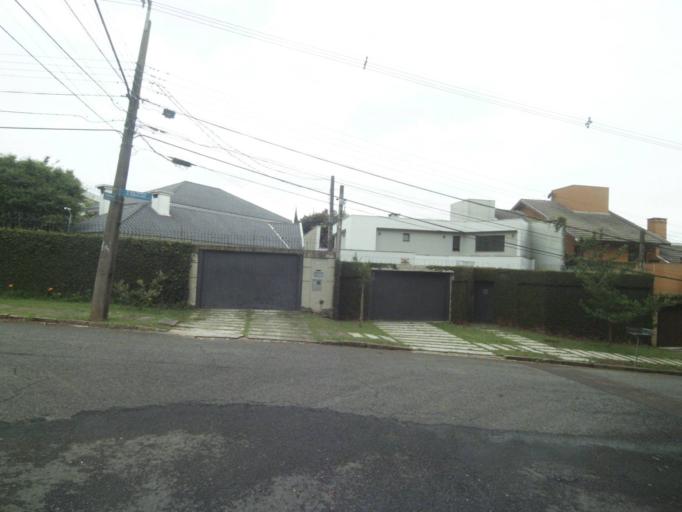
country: BR
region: Parana
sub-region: Curitiba
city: Curitiba
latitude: -25.4064
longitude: -49.2895
